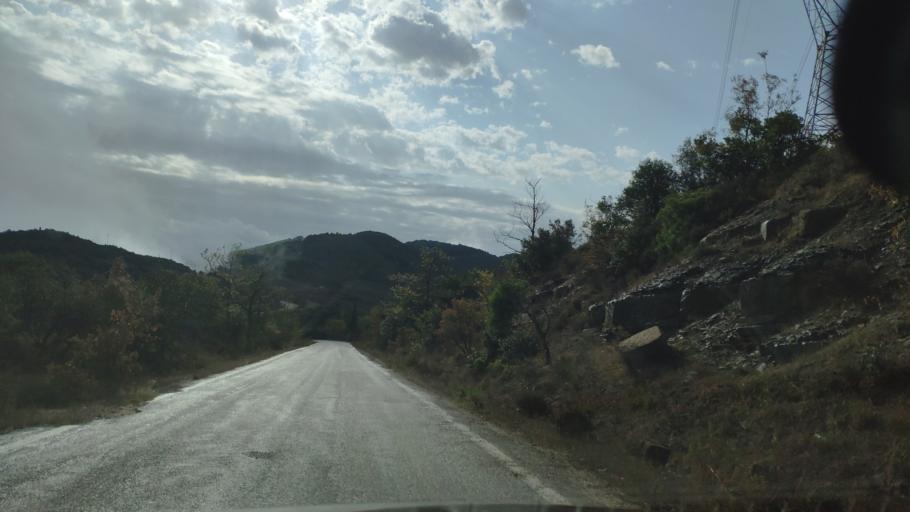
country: GR
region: West Greece
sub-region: Nomos Aitolias kai Akarnanias
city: Sardinia
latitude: 38.8742
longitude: 21.2742
